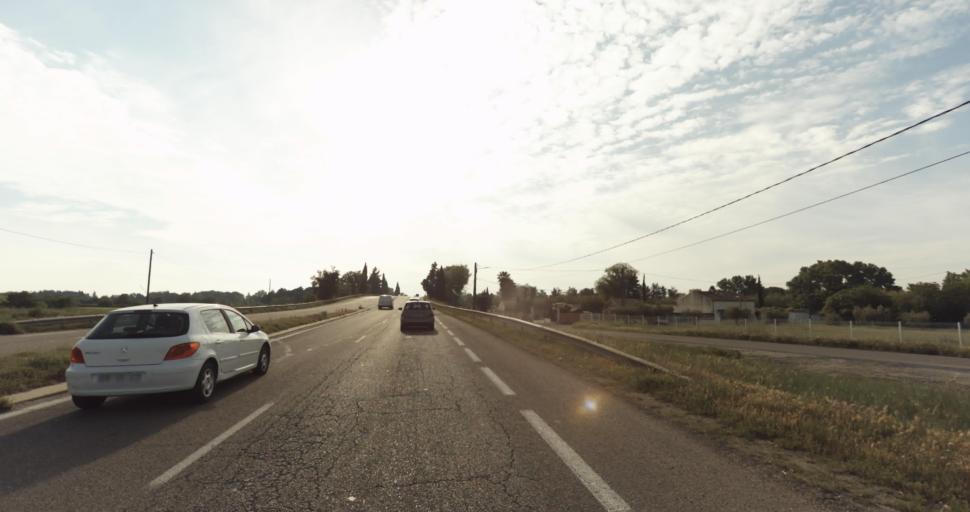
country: FR
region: Languedoc-Roussillon
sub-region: Departement du Gard
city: Rodilhan
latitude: 43.8354
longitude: 4.4035
